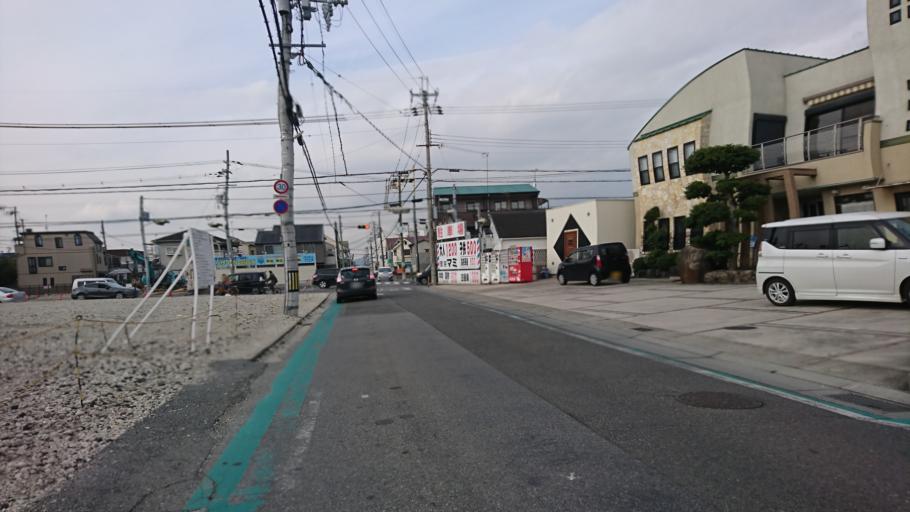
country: JP
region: Hyogo
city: Kakogawacho-honmachi
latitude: 34.7737
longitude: 134.8467
